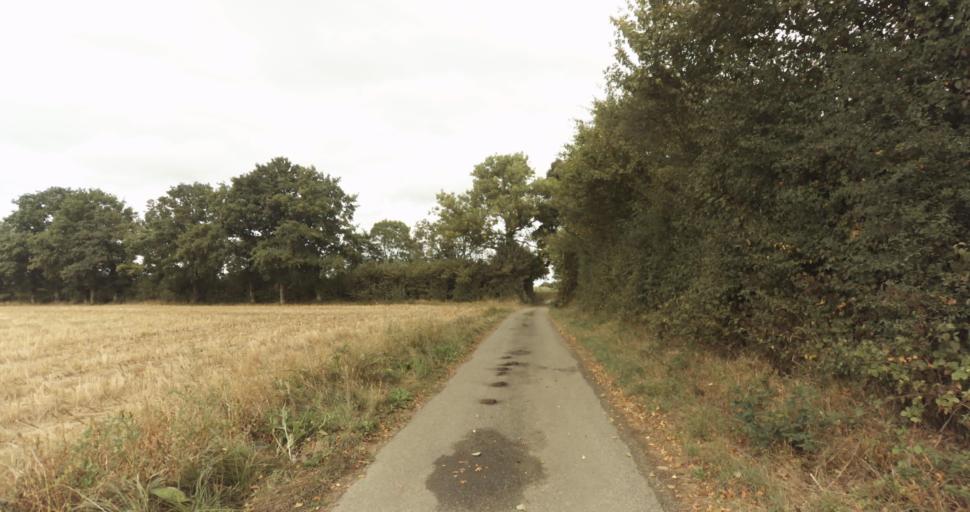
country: FR
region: Lower Normandy
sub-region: Departement de l'Orne
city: Gace
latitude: 48.8493
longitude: 0.2565
